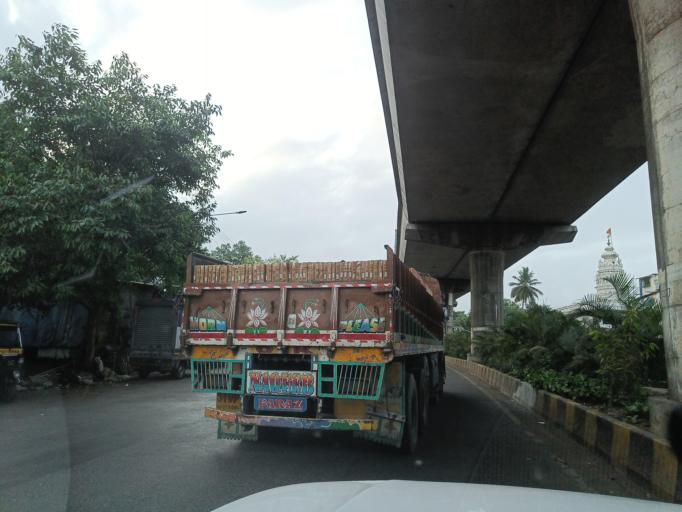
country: IN
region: Maharashtra
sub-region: Mumbai Suburban
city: Powai
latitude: 19.0938
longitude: 72.8989
